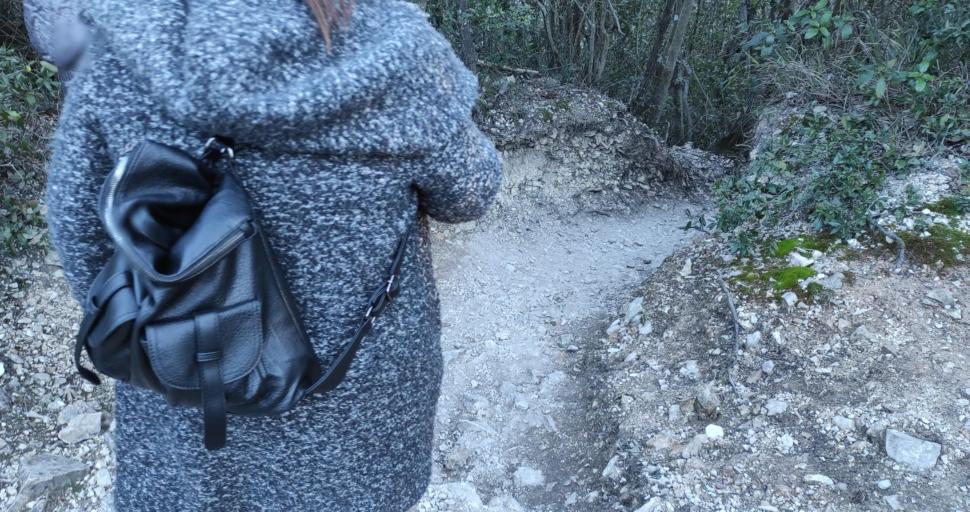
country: IT
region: The Marches
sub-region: Provincia di Ancona
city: Sirolo
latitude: 43.5460
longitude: 13.6202
